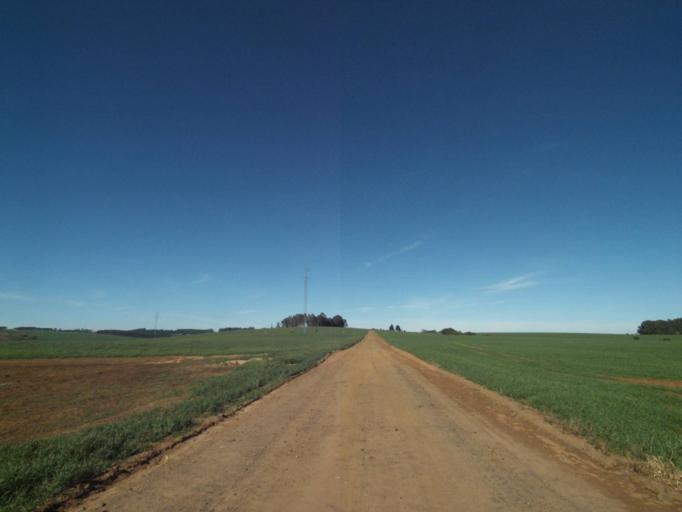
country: BR
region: Parana
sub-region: Tibagi
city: Tibagi
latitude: -24.5761
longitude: -50.2655
